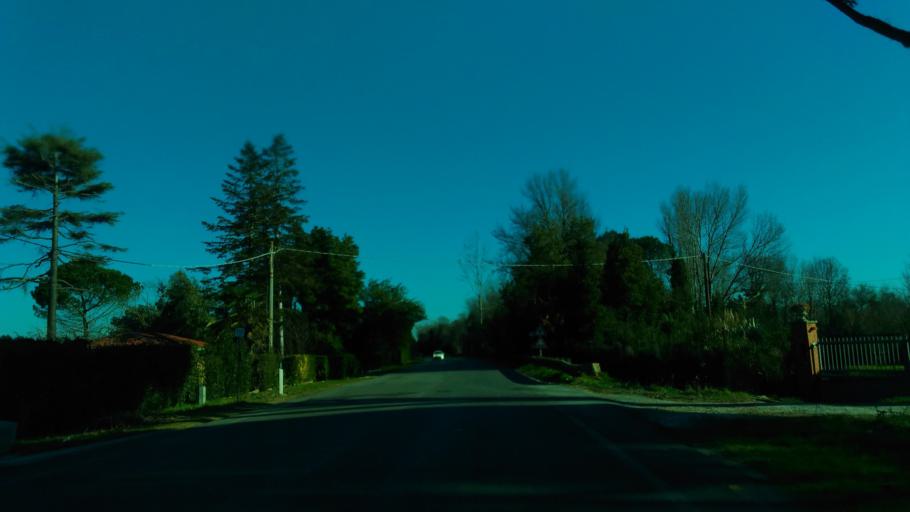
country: IT
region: Tuscany
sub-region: Province of Pisa
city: Marina di Pisa
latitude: 43.6773
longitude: 10.3036
